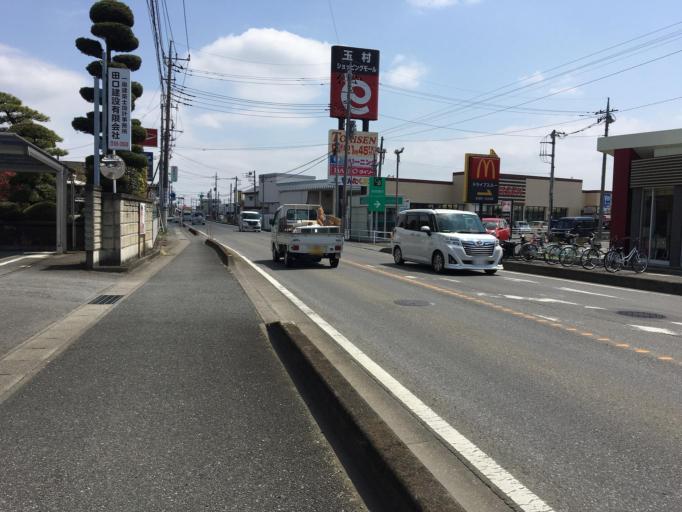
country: JP
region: Gunma
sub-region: Sawa-gun
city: Tamamura
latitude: 36.3024
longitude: 139.1264
